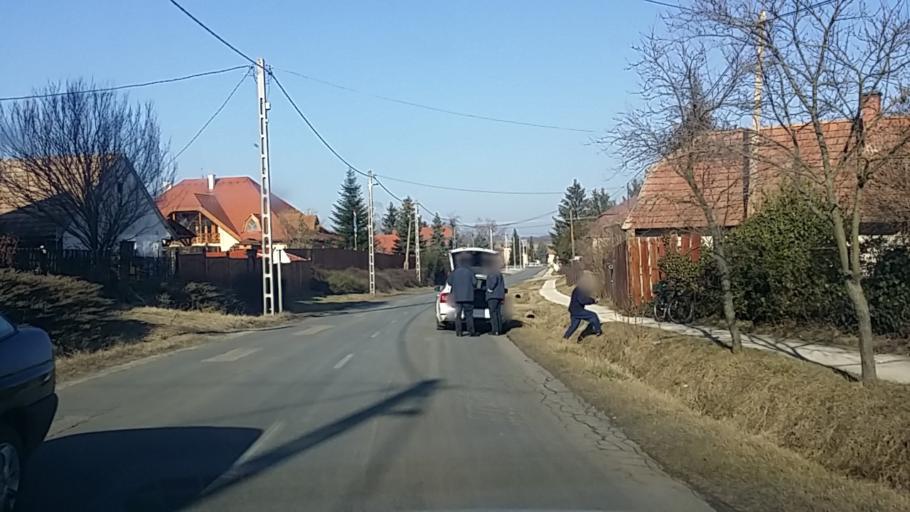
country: HU
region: Komarom-Esztergom
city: Bokod
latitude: 47.5164
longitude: 18.2258
